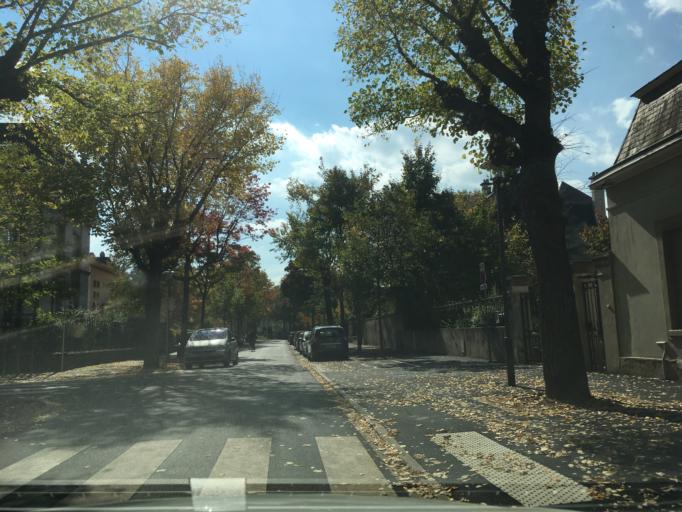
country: FR
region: Alsace
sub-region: Departement du Haut-Rhin
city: Colmar
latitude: 48.0704
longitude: 7.3491
